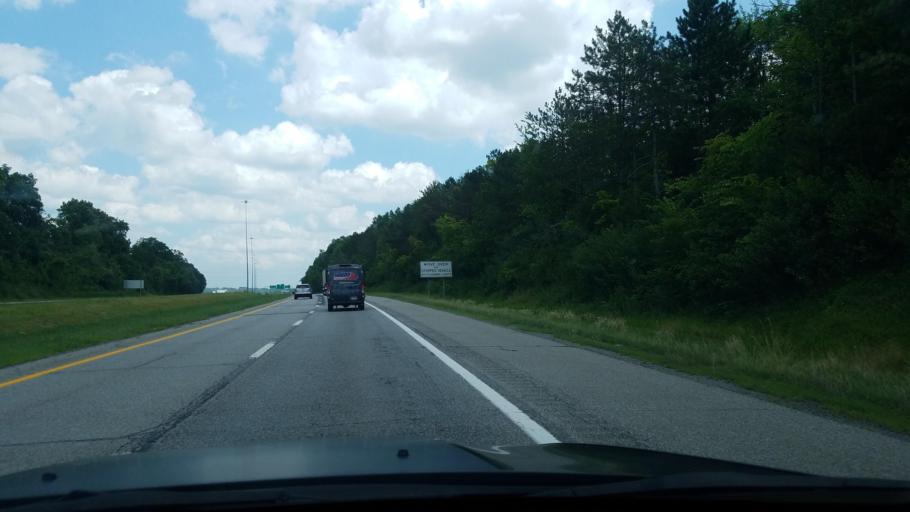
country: US
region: Ohio
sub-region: Trumbull County
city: Girard
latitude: 41.1230
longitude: -80.7250
